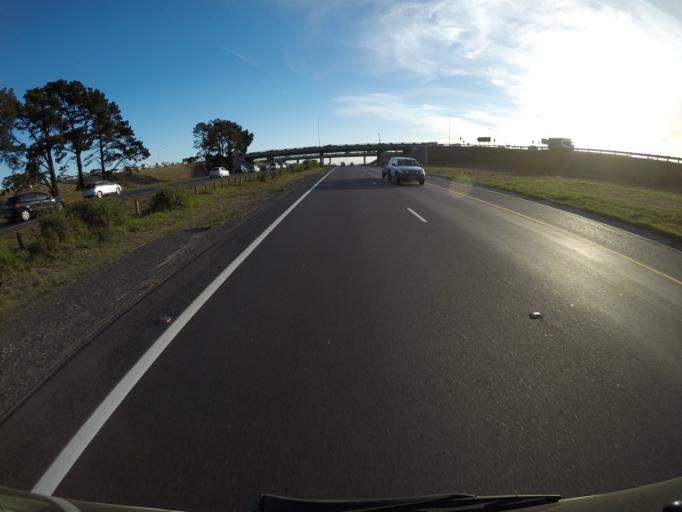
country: ZA
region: Western Cape
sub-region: City of Cape Town
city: Kraaifontein
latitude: -33.8570
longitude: 18.6968
